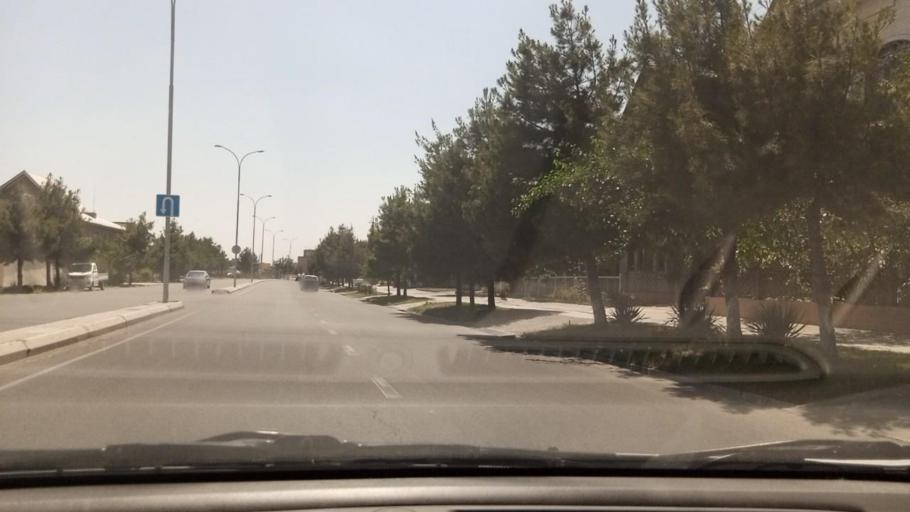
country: UZ
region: Toshkent Shahri
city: Tashkent
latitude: 41.2304
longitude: 69.1841
